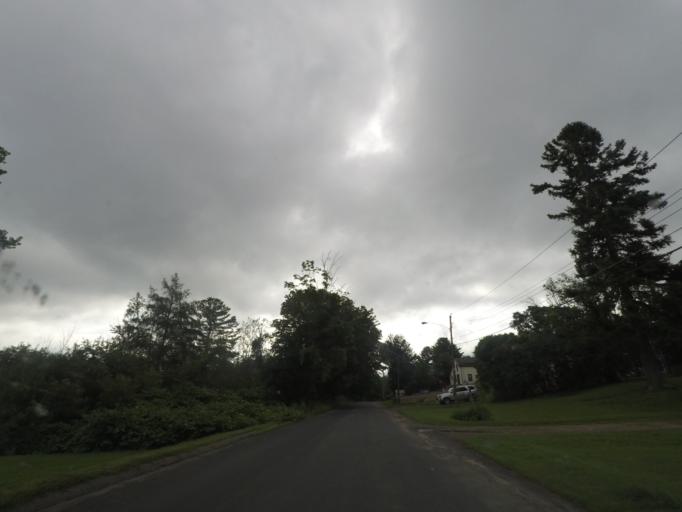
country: US
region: Massachusetts
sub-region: Berkshire County
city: Pittsfield
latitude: 42.4241
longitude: -73.3123
